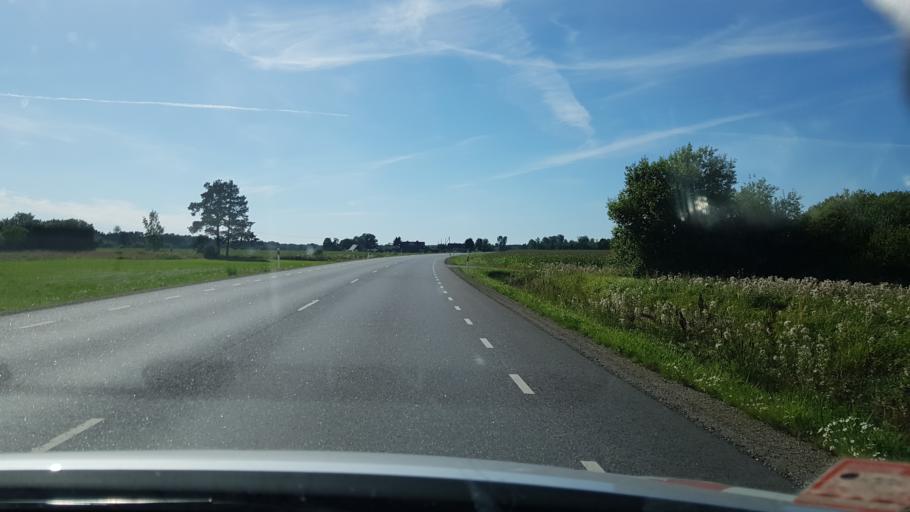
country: EE
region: Tartu
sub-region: UElenurme vald
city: Ulenurme
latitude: 58.1769
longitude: 26.8666
